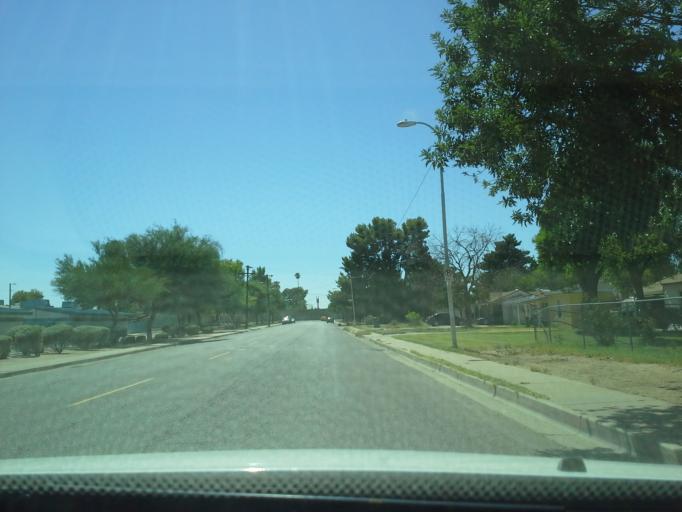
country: US
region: Arizona
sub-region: Maricopa County
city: Phoenix
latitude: 33.5169
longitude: -112.1095
